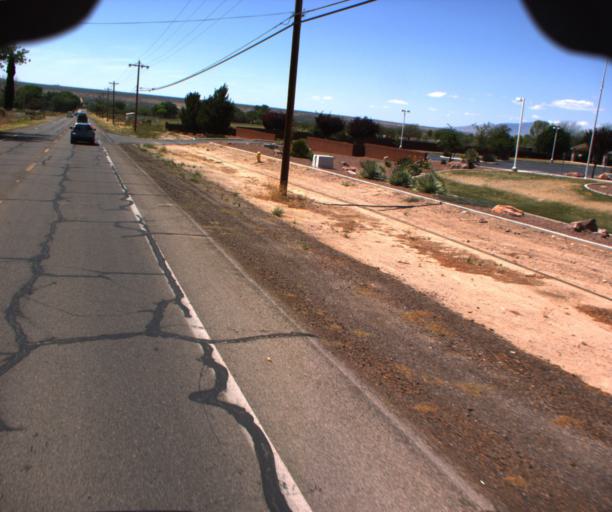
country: US
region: Arizona
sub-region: Cochise County
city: Saint David
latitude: 31.9054
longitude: -110.2358
